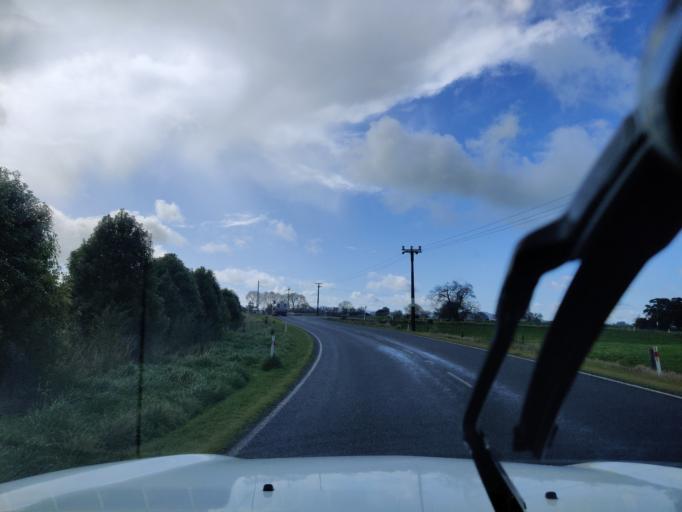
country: NZ
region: Waikato
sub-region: Waikato District
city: Ngaruawahia
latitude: -37.5682
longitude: 175.2618
